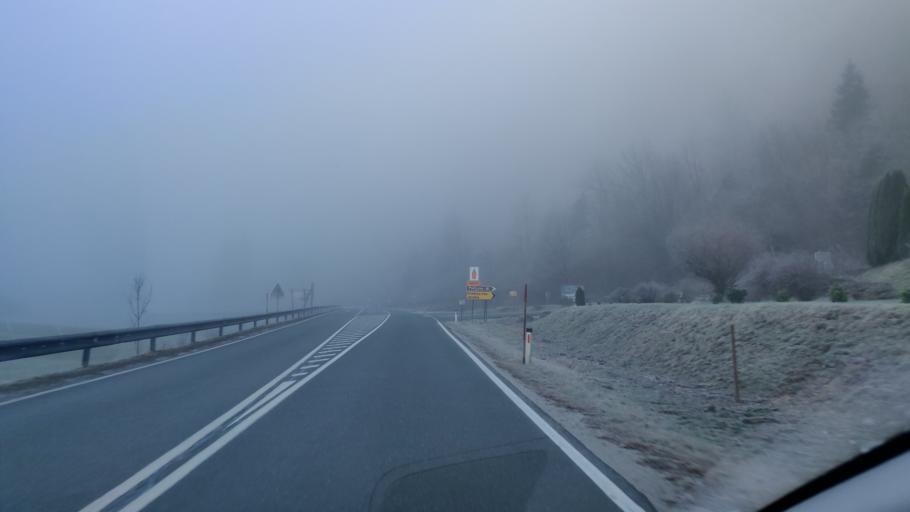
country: SI
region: Bohinj
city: Bohinjska Bistrica
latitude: 46.2827
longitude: 13.9568
